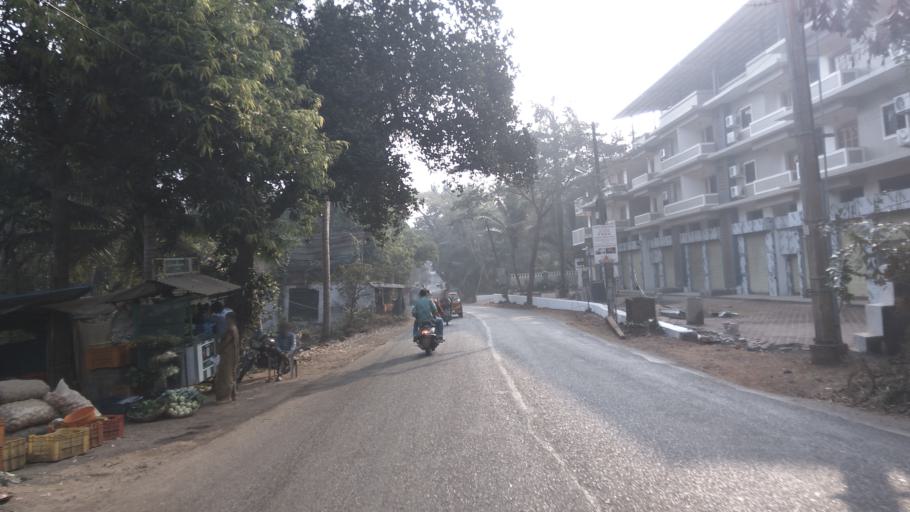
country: IN
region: Goa
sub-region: North Goa
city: Saligao
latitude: 15.5433
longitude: 73.8115
